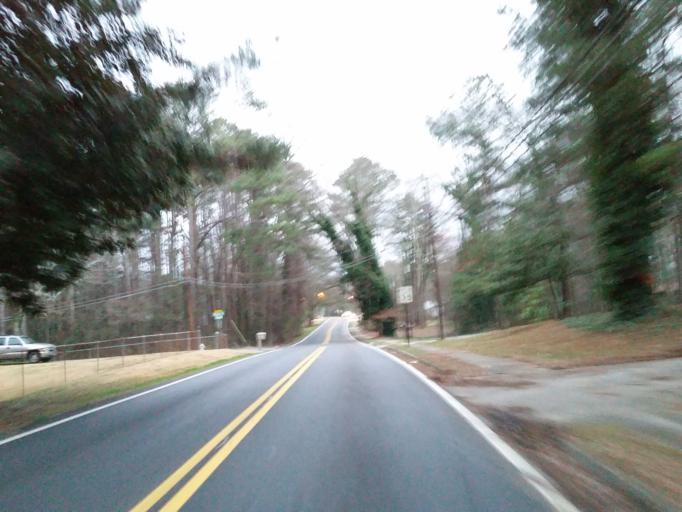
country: US
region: Georgia
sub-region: Cobb County
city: Mableton
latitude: 33.8449
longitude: -84.5775
